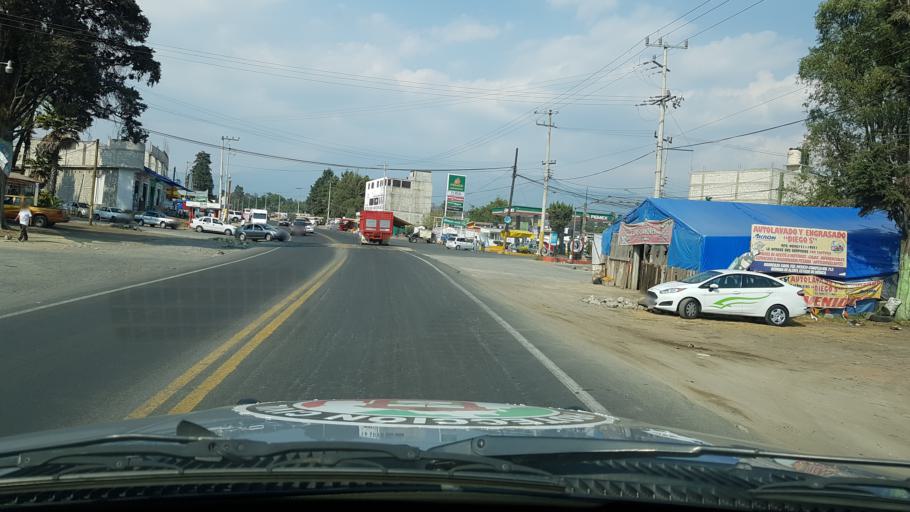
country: MX
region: Mexico
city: Ozumba de Alzate
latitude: 19.0464
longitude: -98.7946
